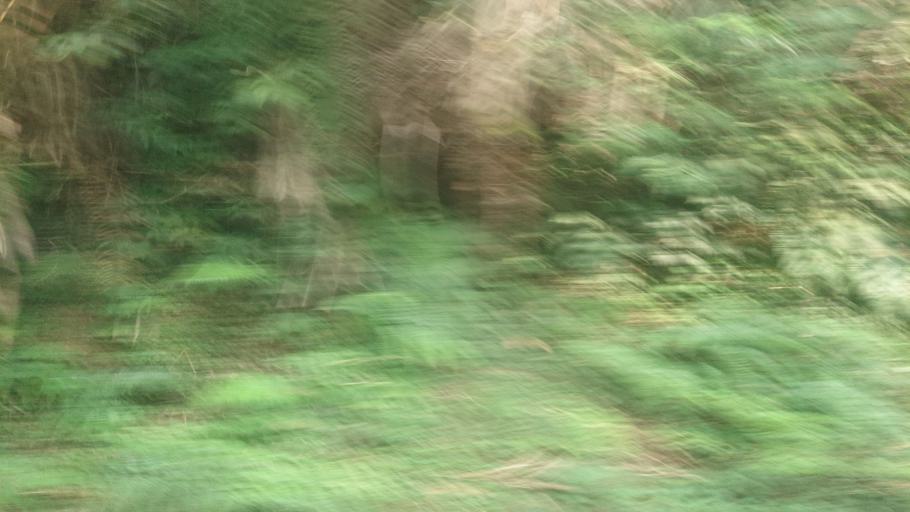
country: TW
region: Taiwan
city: Lugu
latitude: 23.5028
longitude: 120.7835
